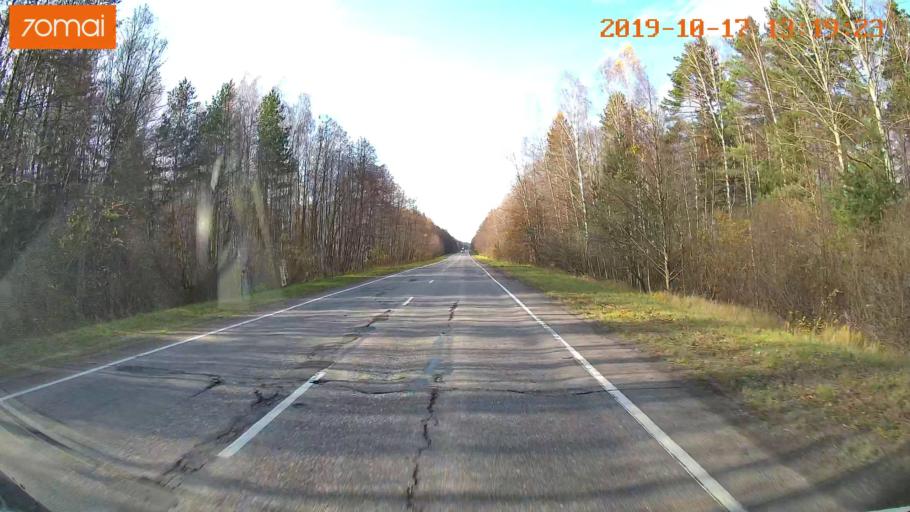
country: RU
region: Rjazan
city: Gus'-Zheleznyy
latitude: 55.0690
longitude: 41.0755
